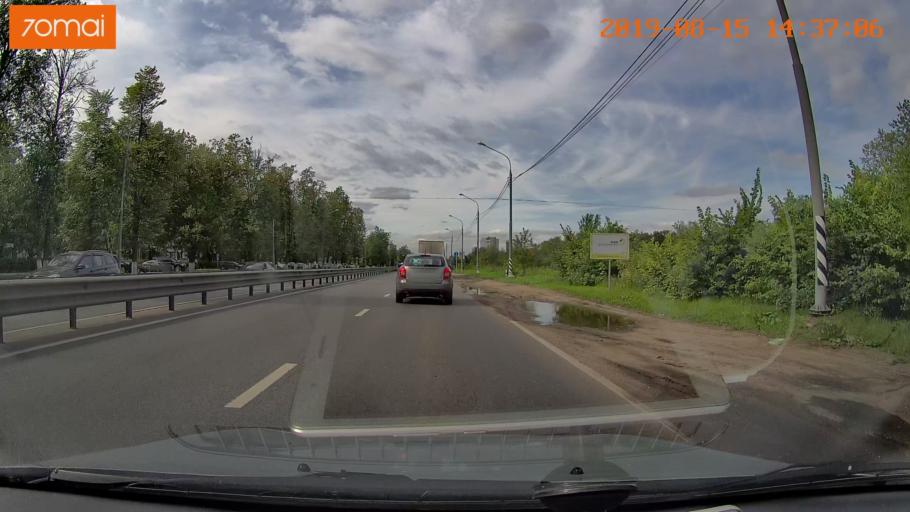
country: RU
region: Moskovskaya
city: Tomilino
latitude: 55.6508
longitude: 37.9298
